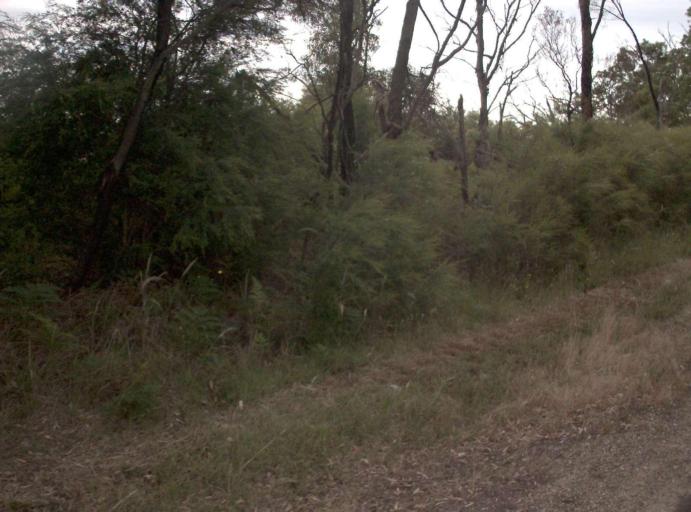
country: AU
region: Victoria
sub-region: Wellington
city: Sale
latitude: -38.0057
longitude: 147.2822
